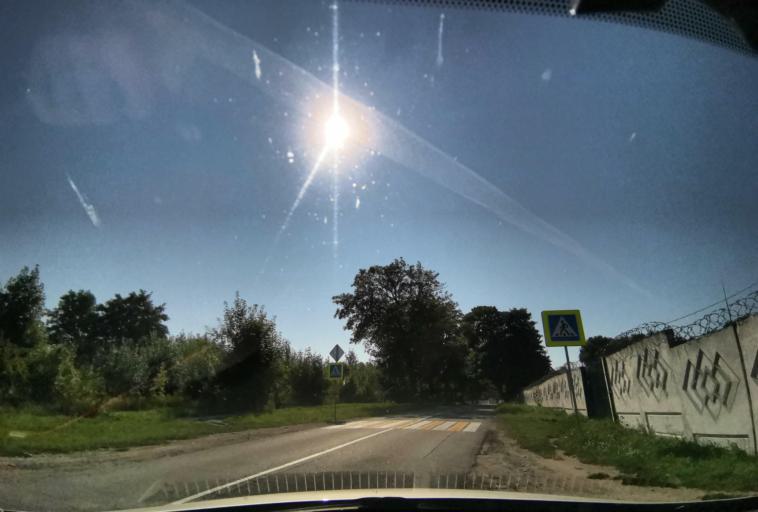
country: RU
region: Kaliningrad
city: Primorsk
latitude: 54.7426
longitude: 20.0059
